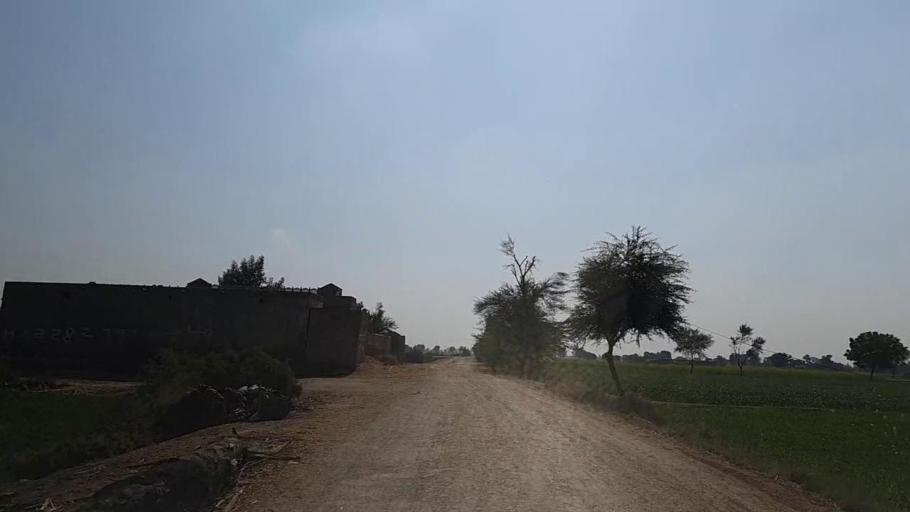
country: PK
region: Sindh
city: Daur
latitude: 26.4568
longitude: 68.2631
